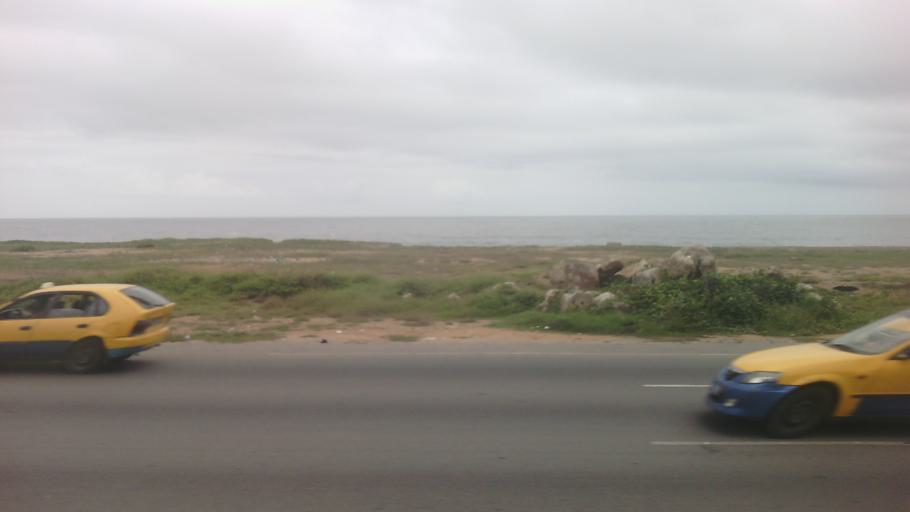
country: CI
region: Lagunes
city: Abidjan
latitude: 5.2453
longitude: -3.9339
